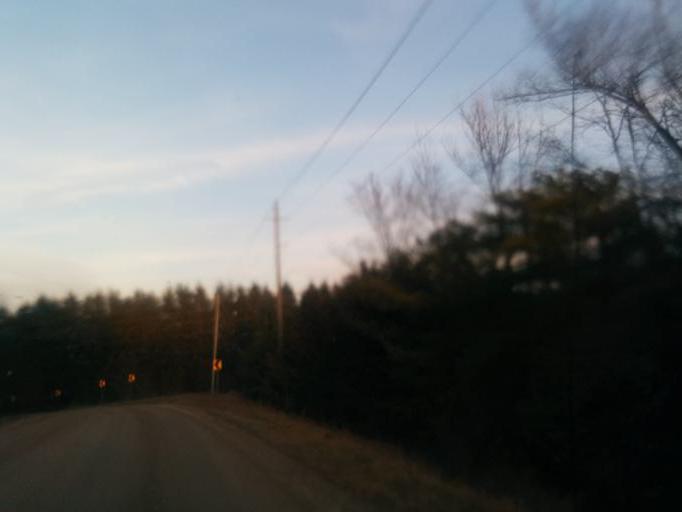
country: CA
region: Ontario
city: Orangeville
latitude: 43.9698
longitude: -79.9743
